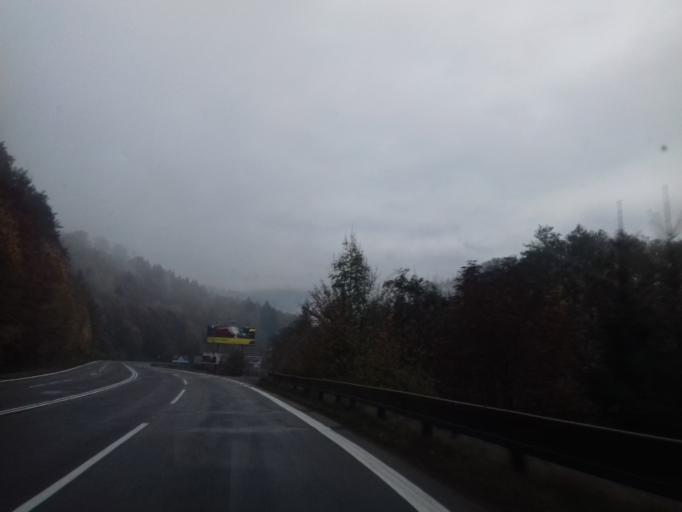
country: SK
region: Banskobystricky
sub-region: Okres Banska Bystrica
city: Banska Bystrica
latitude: 48.7819
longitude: 19.1134
